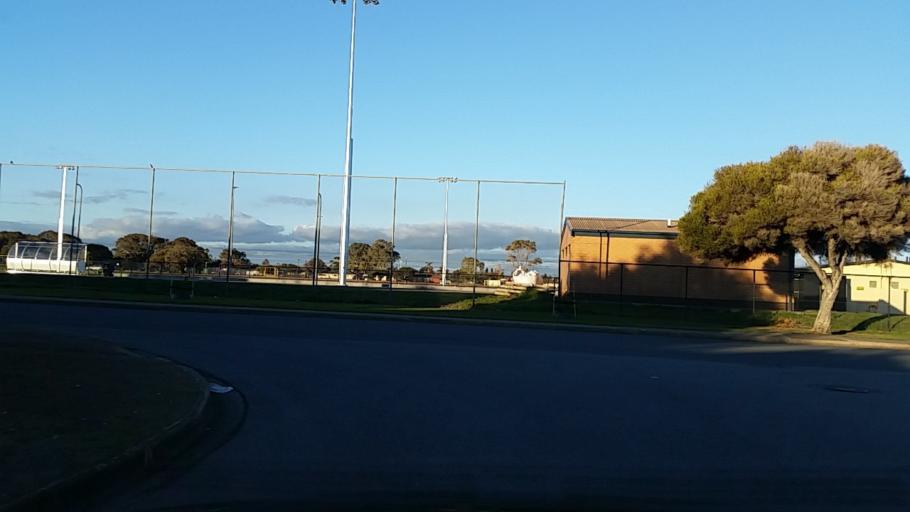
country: AU
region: South Australia
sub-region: Onkaparinga
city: Seaford
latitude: -35.1743
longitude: 138.4700
